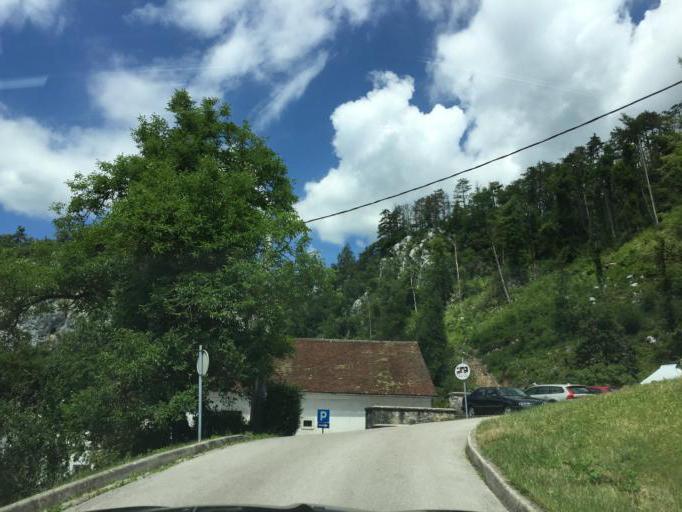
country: SI
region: Postojna
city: Postojna
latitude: 45.8142
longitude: 14.1290
